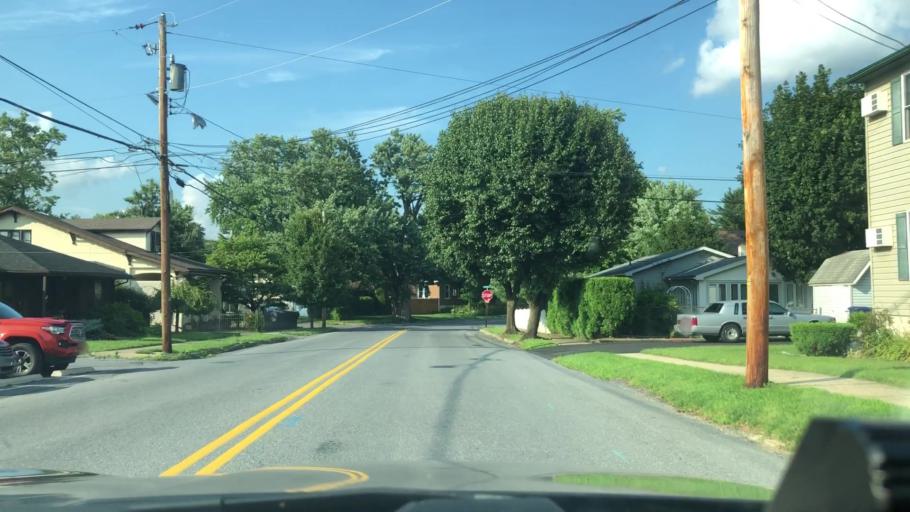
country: US
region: Pennsylvania
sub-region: Lehigh County
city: Allentown
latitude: 40.6172
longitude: -75.5080
